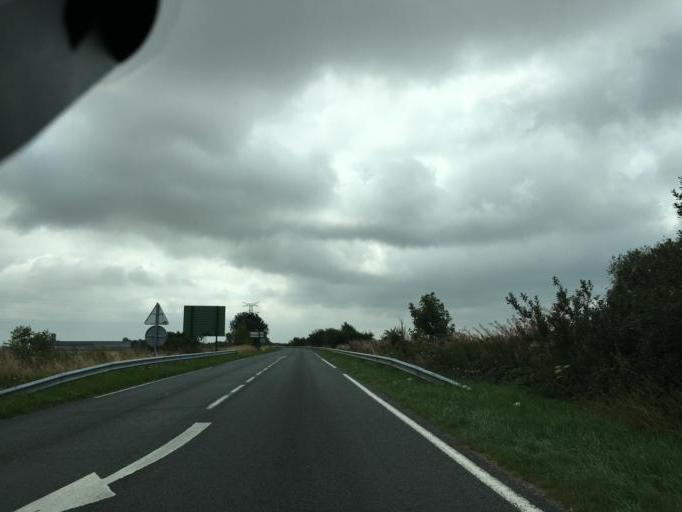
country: FR
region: Nord-Pas-de-Calais
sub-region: Departement du Pas-de-Calais
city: Montreuil
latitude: 50.4398
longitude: 1.7267
